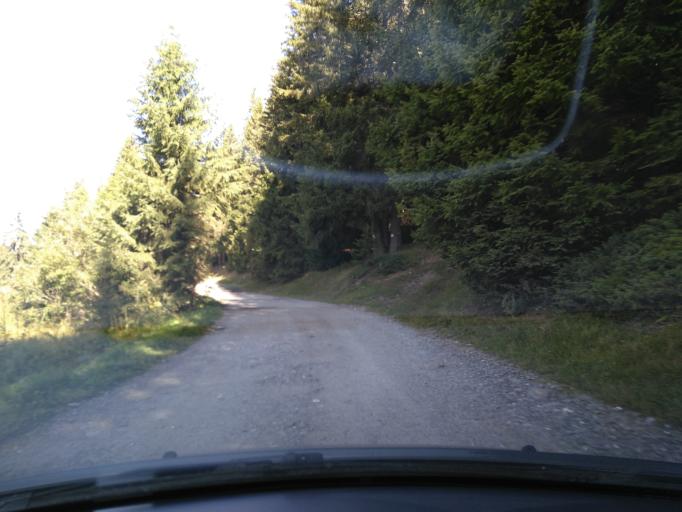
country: FR
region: Rhone-Alpes
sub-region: Departement de la Haute-Savoie
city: Praz-sur-Arly
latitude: 45.7832
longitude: 6.5246
